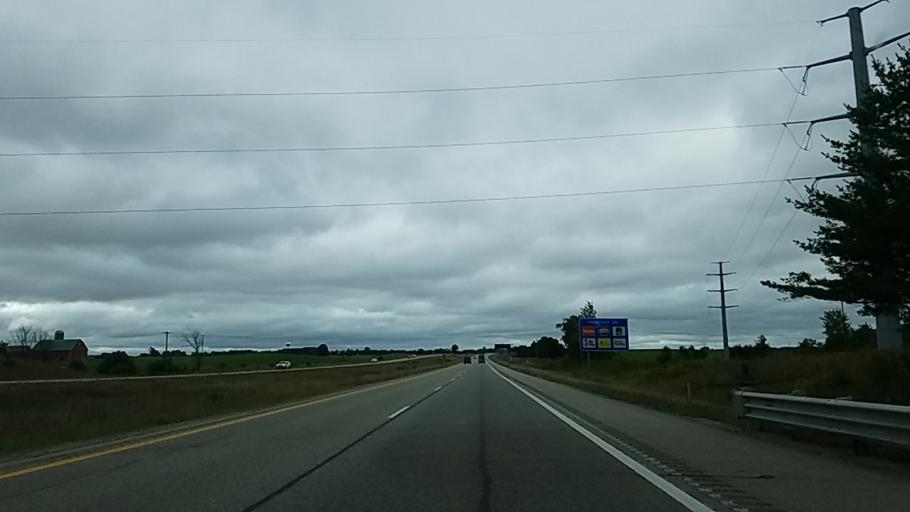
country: US
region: Michigan
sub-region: Otsego County
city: Gaylord
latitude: 45.0582
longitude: -84.6885
